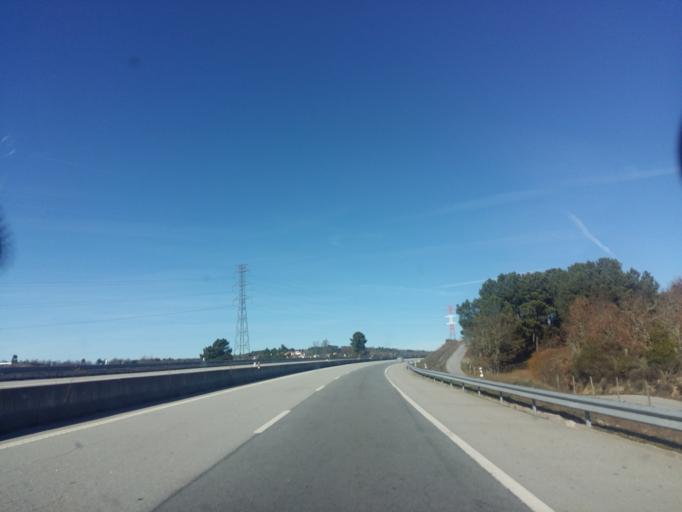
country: PT
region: Guarda
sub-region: Guarda
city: Sequeira
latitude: 40.5497
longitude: -7.2168
